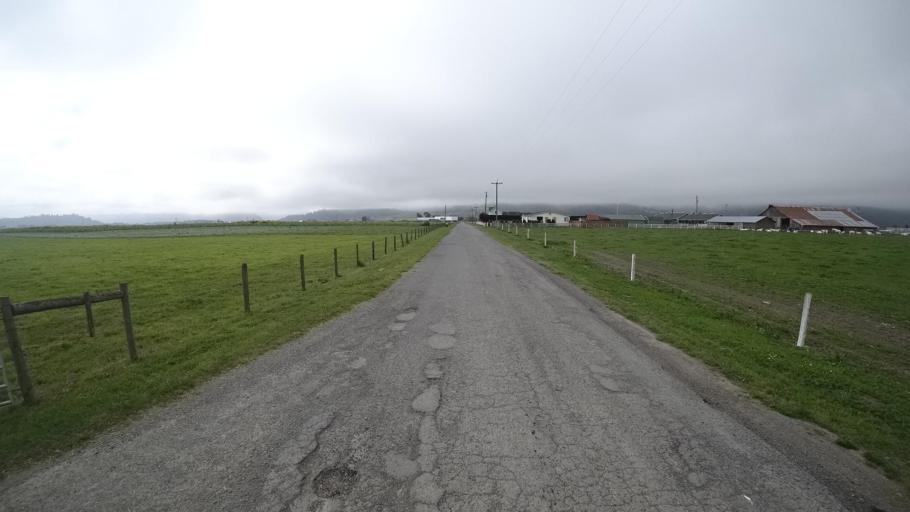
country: US
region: California
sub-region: Humboldt County
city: Fortuna
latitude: 40.5775
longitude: -124.1878
